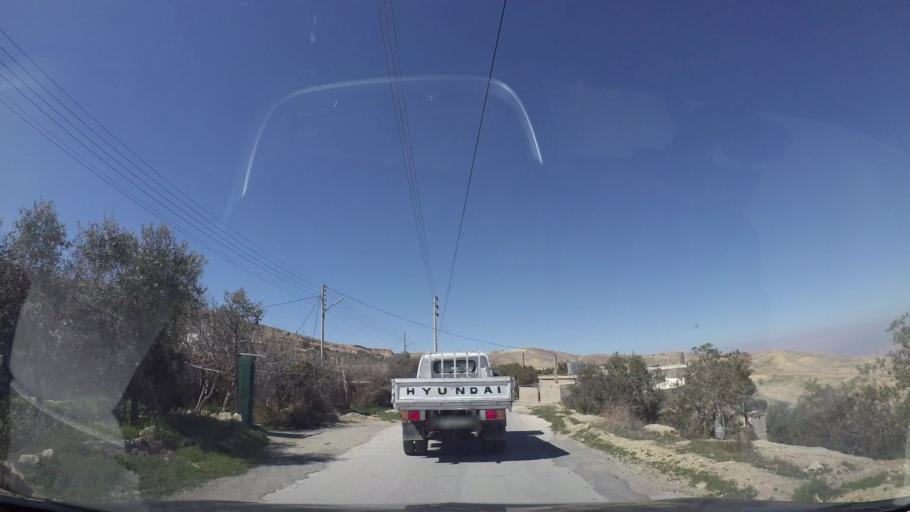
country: JO
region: Tafielah
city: At Tafilah
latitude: 30.8394
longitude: 35.5719
